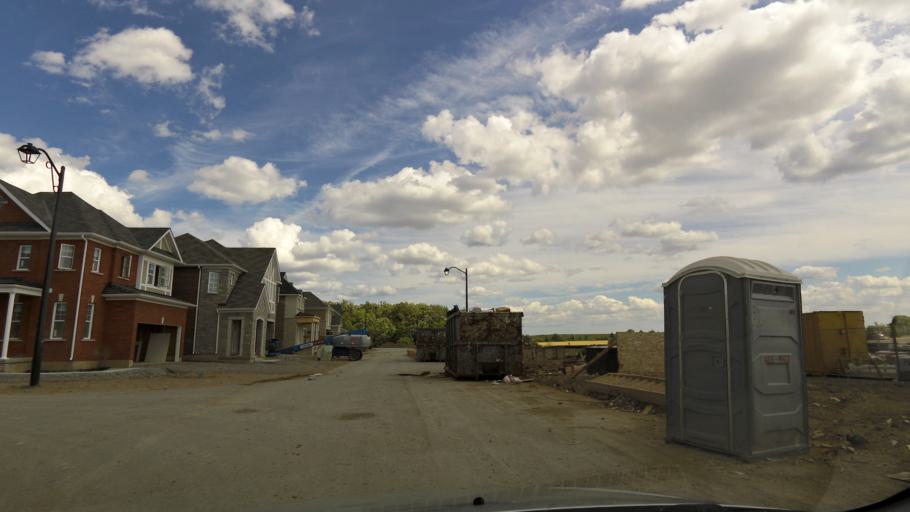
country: CA
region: Ontario
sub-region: Halton
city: Milton
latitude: 43.4834
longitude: -79.8409
